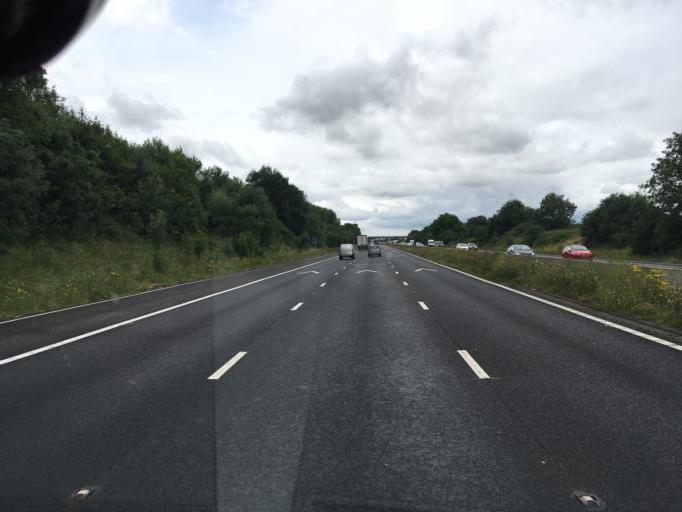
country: GB
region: England
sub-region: Gloucestershire
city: Barnwood
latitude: 51.8260
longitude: -2.2135
